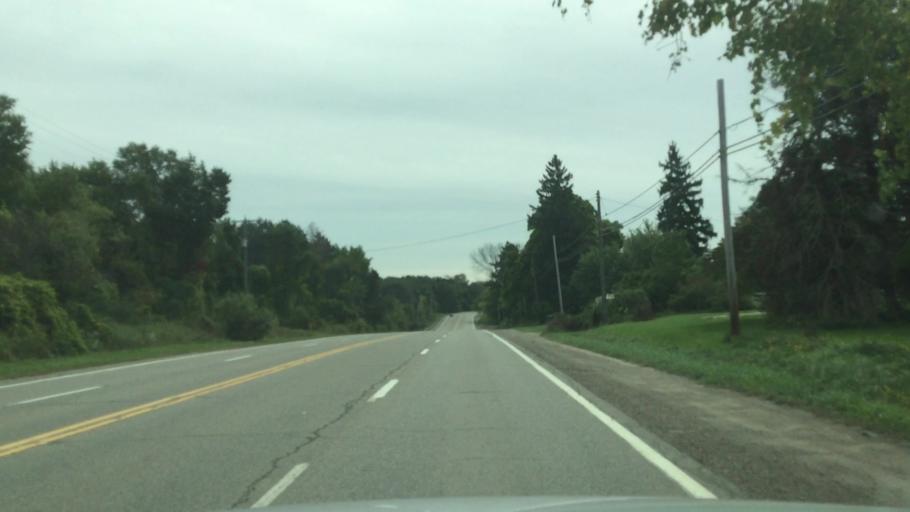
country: US
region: Michigan
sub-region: Oakland County
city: Holly
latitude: 42.8131
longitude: -83.5430
